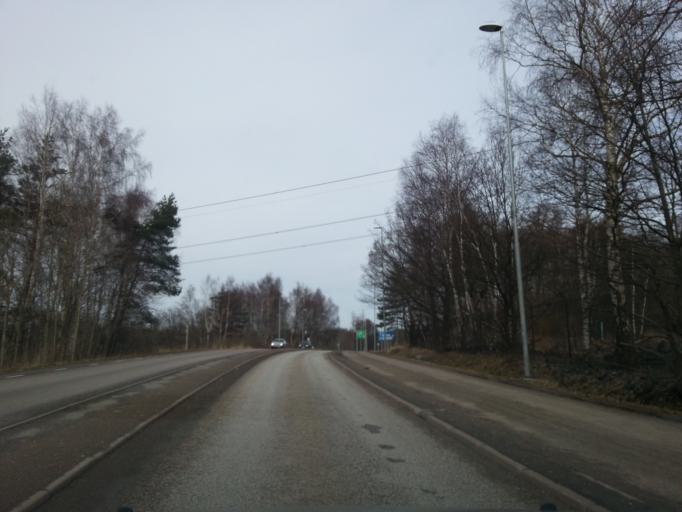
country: SE
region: Vaestra Goetaland
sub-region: Goteborg
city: Hammarkullen
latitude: 57.7582
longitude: 12.0106
